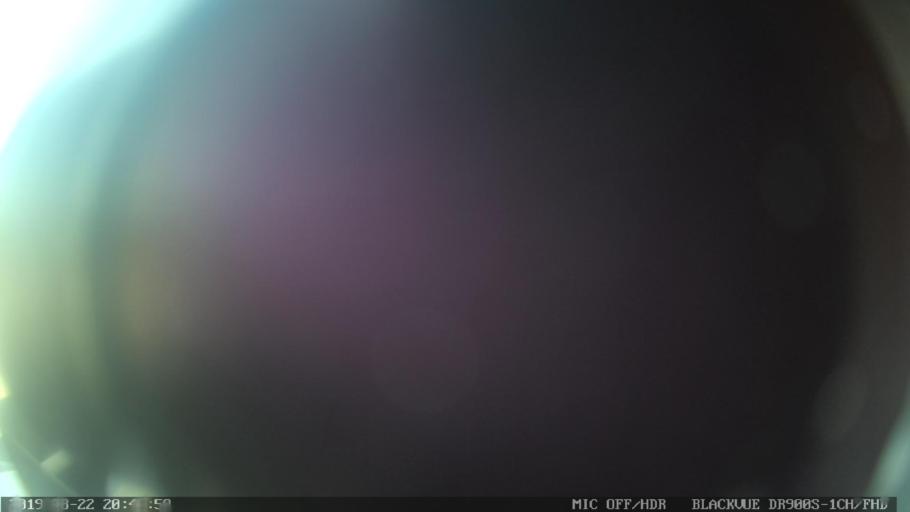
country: PT
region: Castelo Branco
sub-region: Proenca-A-Nova
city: Proenca-a-Nova
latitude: 39.6893
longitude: -7.8089
